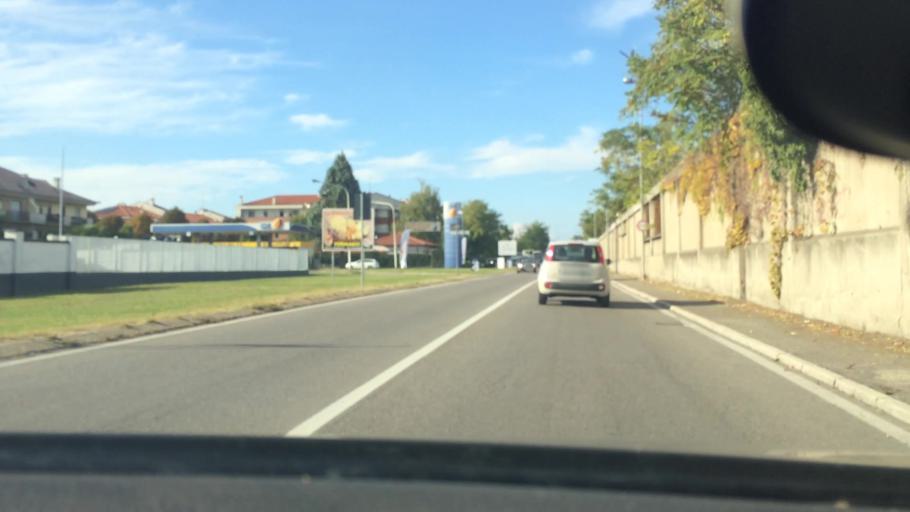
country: IT
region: Lombardy
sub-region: Citta metropolitana di Milano
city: Legnano
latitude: 45.5854
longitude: 8.9036
